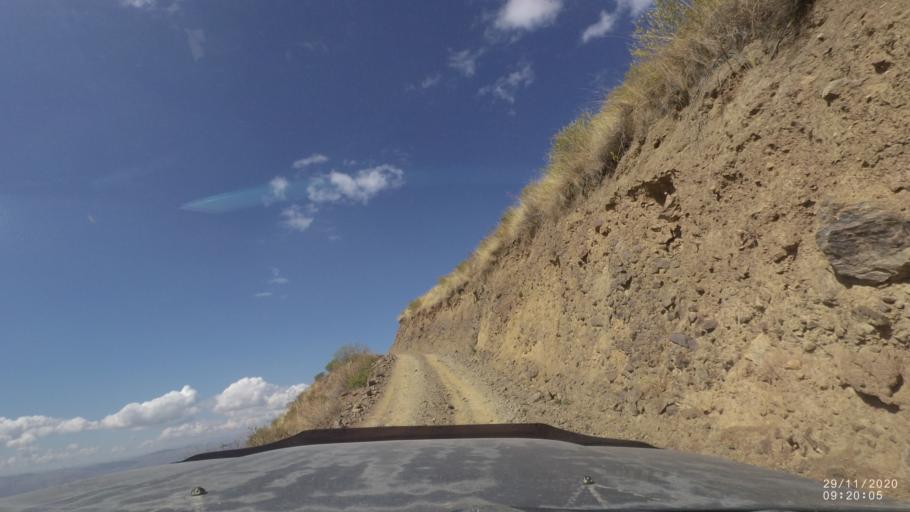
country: BO
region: Cochabamba
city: Cochabamba
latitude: -17.3238
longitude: -66.1851
